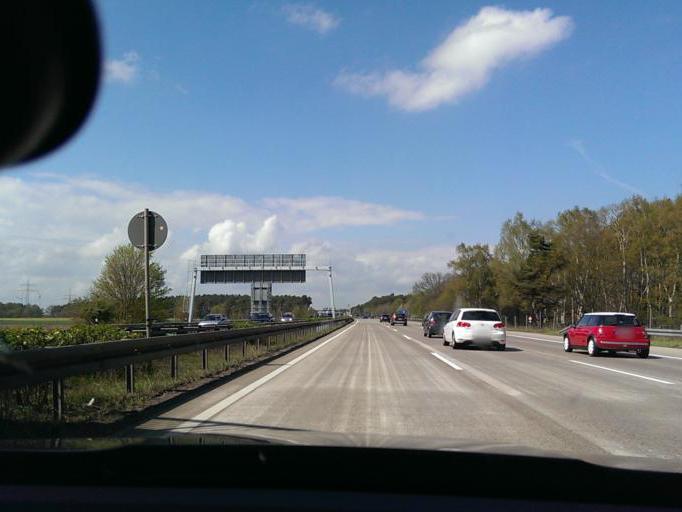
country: DE
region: Lower Saxony
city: Elze
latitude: 52.5634
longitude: 9.7876
